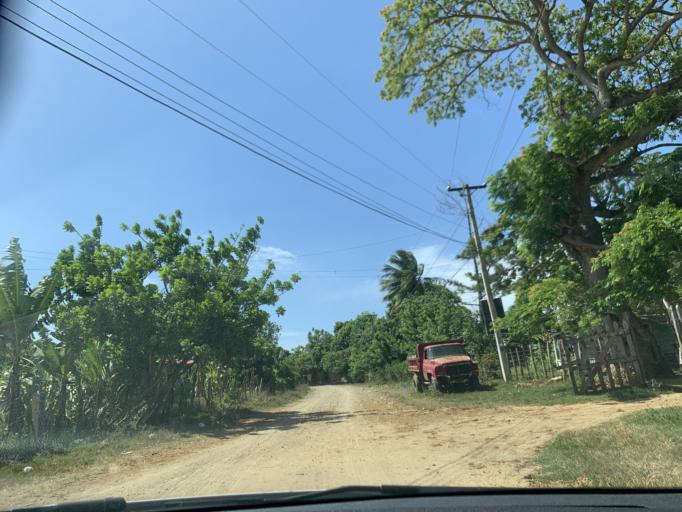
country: DO
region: Puerto Plata
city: Luperon
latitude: 19.8886
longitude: -70.8761
